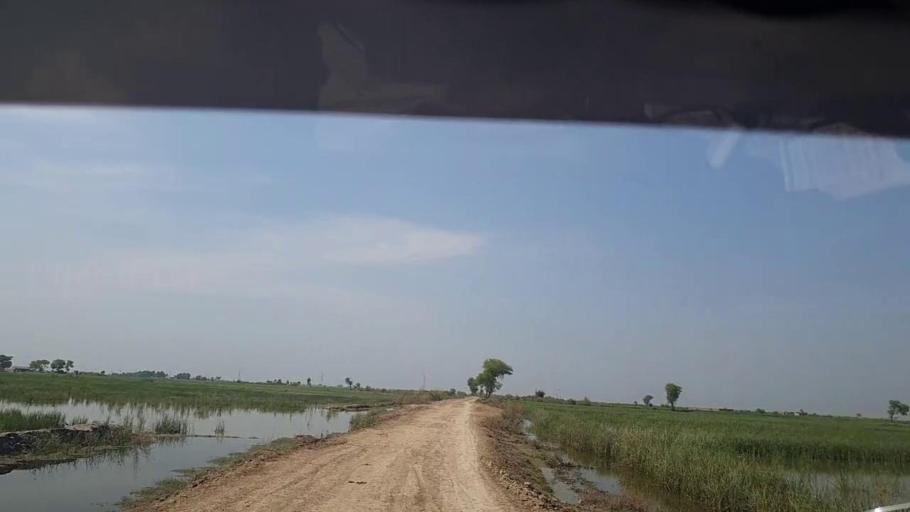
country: PK
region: Sindh
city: Thul
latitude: 28.2173
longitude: 68.6788
